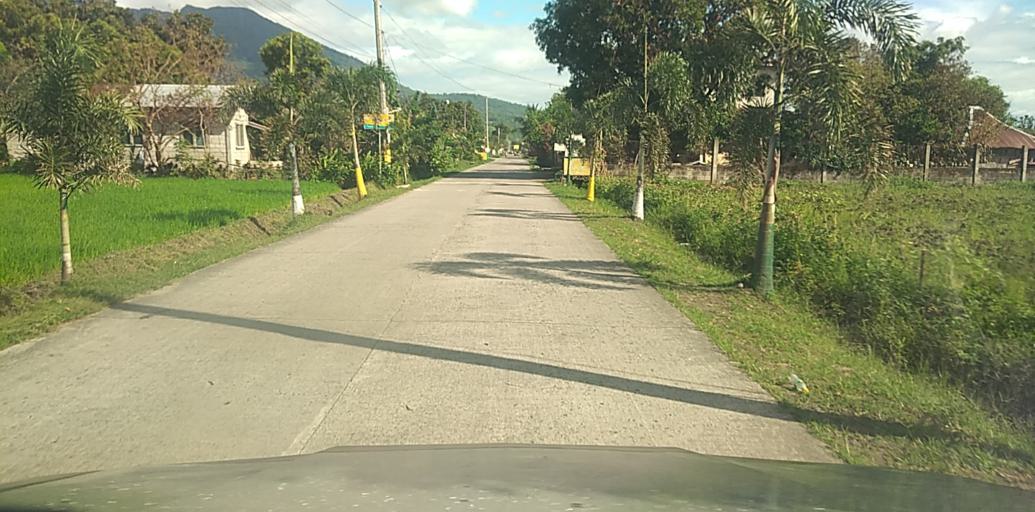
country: PH
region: Central Luzon
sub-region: Province of Pampanga
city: Buensuseso
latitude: 15.1932
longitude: 120.6818
